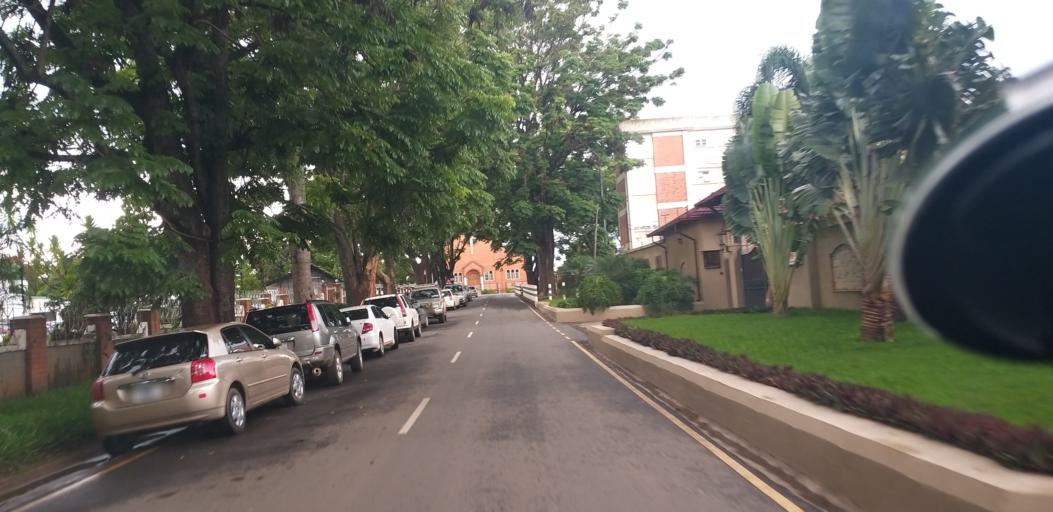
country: ZM
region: Lusaka
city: Lusaka
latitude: -15.4142
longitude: 28.2983
